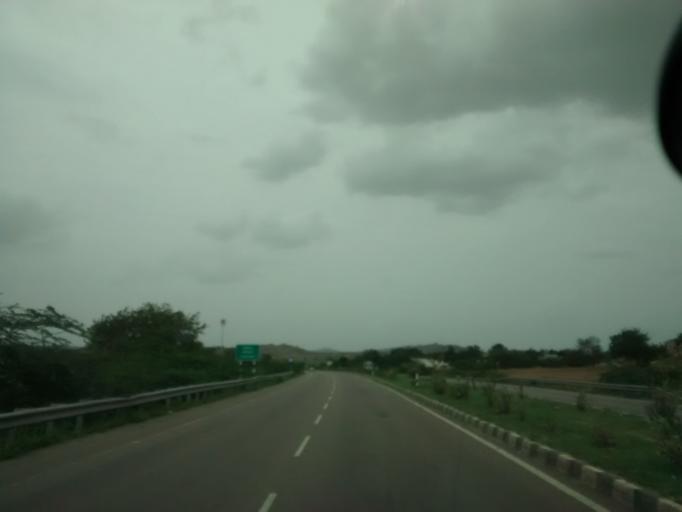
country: IN
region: Andhra Pradesh
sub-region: Kurnool
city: Ramapuram
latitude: 15.1684
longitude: 77.6801
